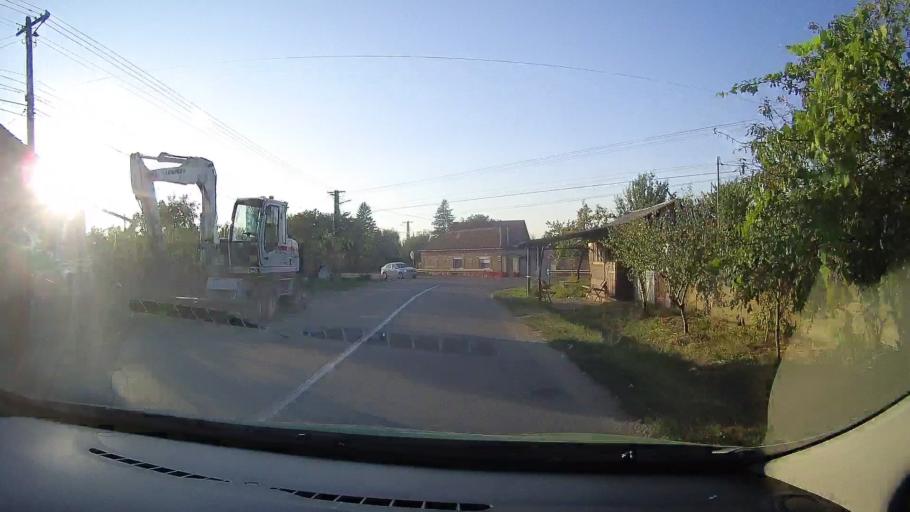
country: RO
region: Bihor
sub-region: Comuna Biharea
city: Biharea
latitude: 47.1649
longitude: 21.9476
